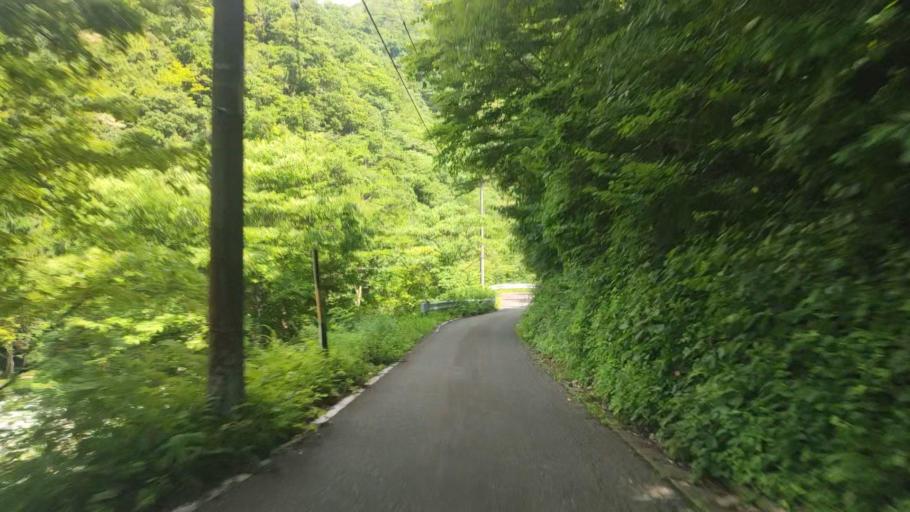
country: JP
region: Fukui
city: Ono
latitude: 35.7447
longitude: 136.5831
